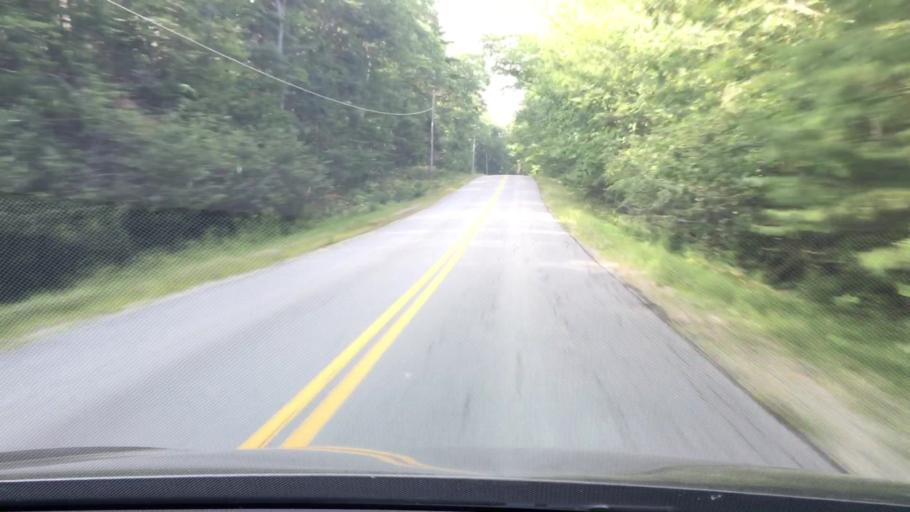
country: US
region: Maine
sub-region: Hancock County
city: Orland
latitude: 44.5273
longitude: -68.7637
